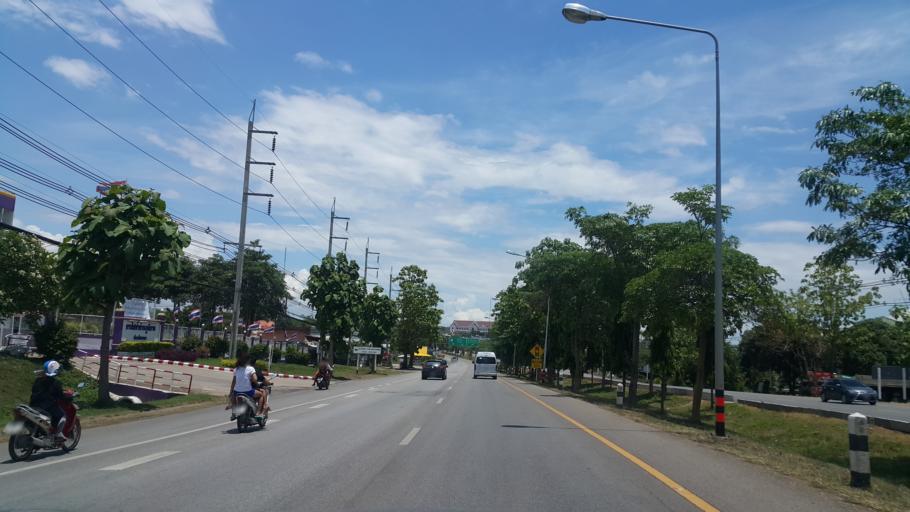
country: TH
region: Phayao
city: Phayao
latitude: 19.1992
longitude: 99.8735
